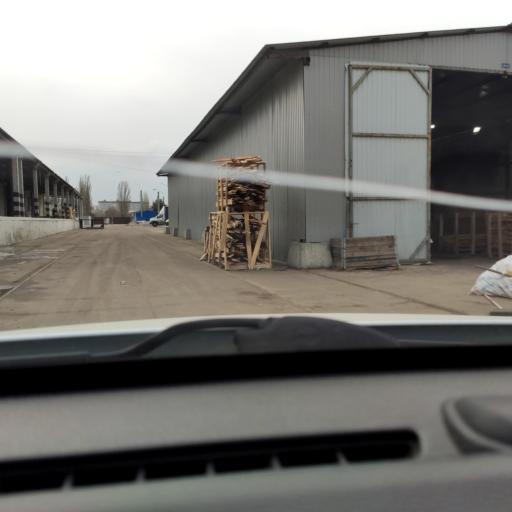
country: RU
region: Voronezj
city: Somovo
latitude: 51.7109
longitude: 39.2895
